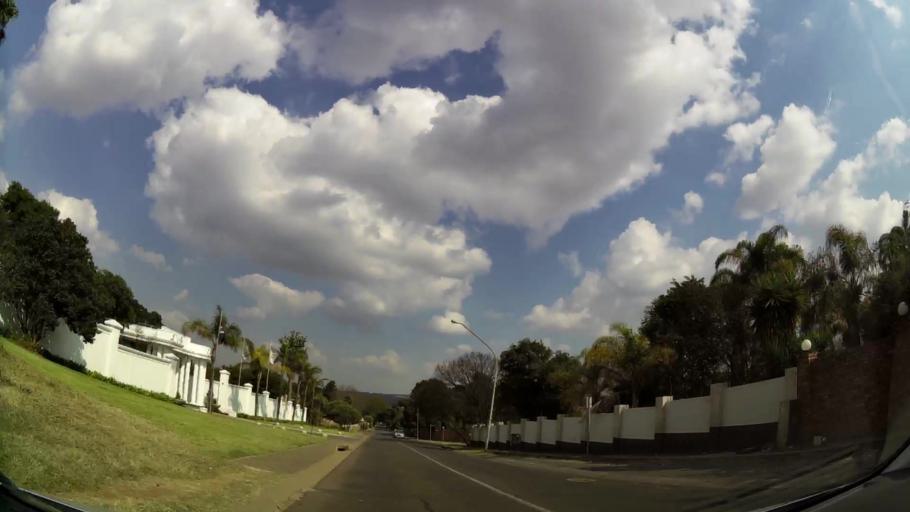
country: ZA
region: Gauteng
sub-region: City of Tshwane Metropolitan Municipality
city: Pretoria
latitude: -25.7789
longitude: 28.3128
